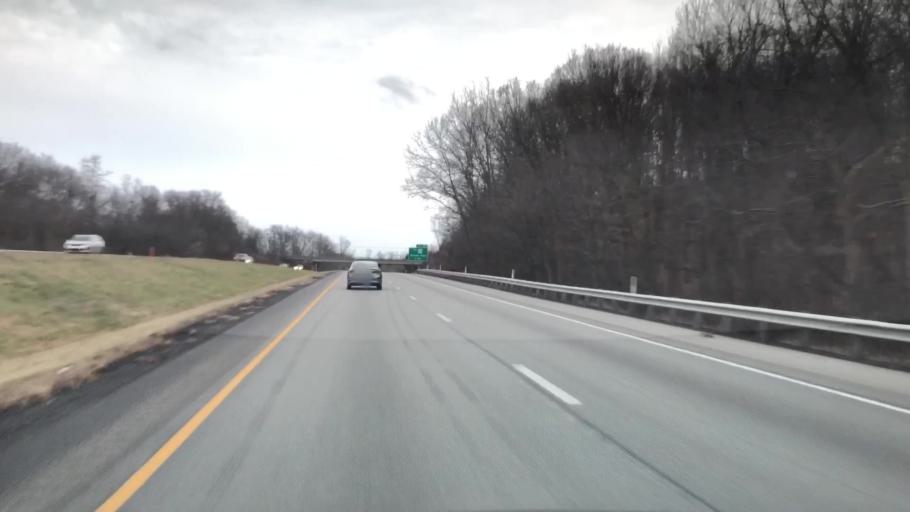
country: US
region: Pennsylvania
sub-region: Butler County
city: Zelienople
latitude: 40.7883
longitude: -80.1245
